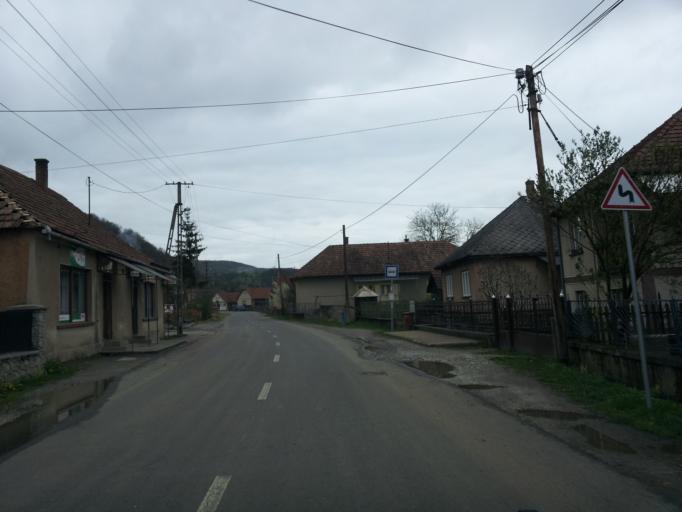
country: HU
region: Borsod-Abauj-Zemplen
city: Rudabanya
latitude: 48.4846
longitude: 20.6250
